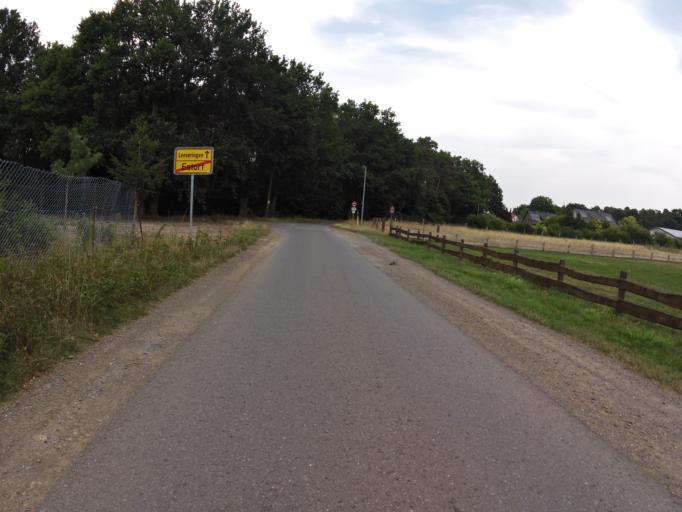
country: DE
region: Lower Saxony
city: Estorf
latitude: 52.5926
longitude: 9.1534
